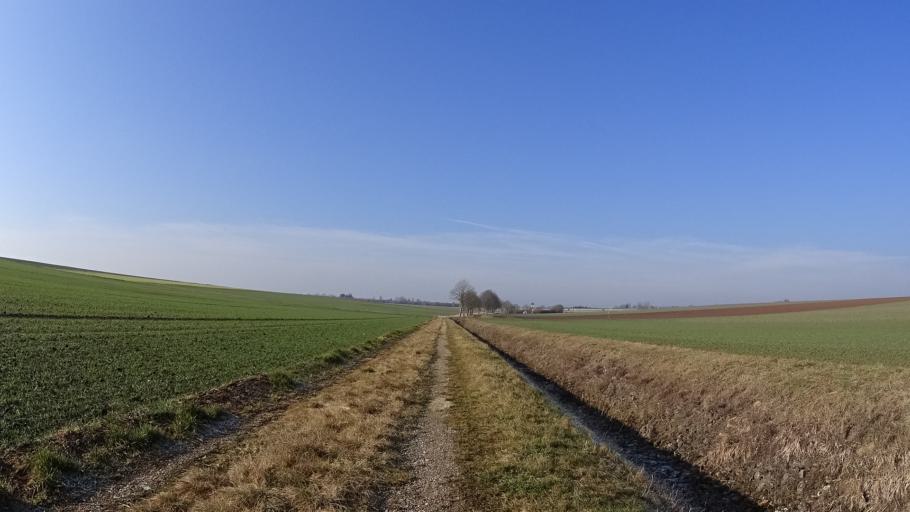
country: DE
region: Bavaria
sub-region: Upper Bavaria
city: Stammham
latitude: 48.8687
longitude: 11.4793
